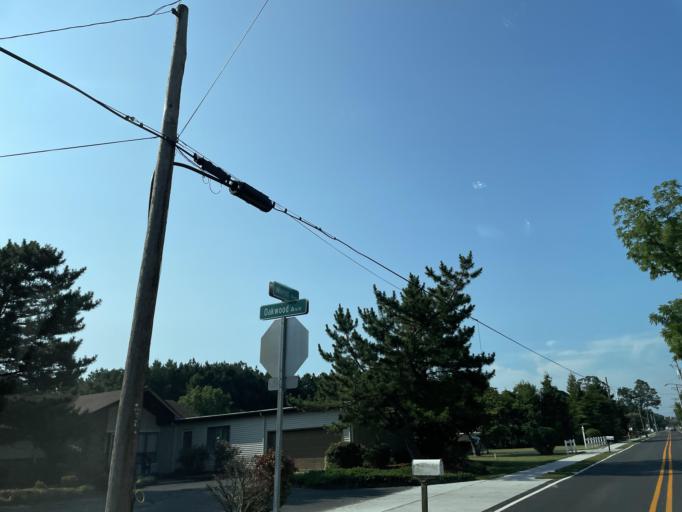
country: US
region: Delaware
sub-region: Sussex County
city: Ocean View
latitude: 38.5471
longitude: -75.0881
